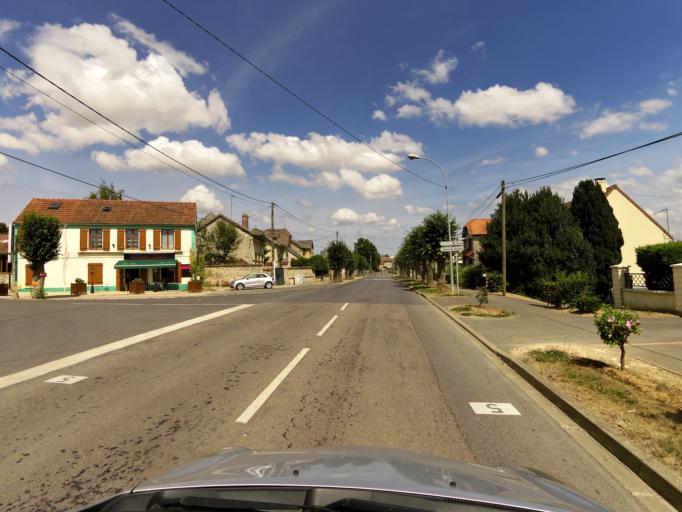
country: FR
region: Picardie
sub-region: Departement de l'Oise
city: Mareuil-sur-Ourcq
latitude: 49.1354
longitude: 3.0769
